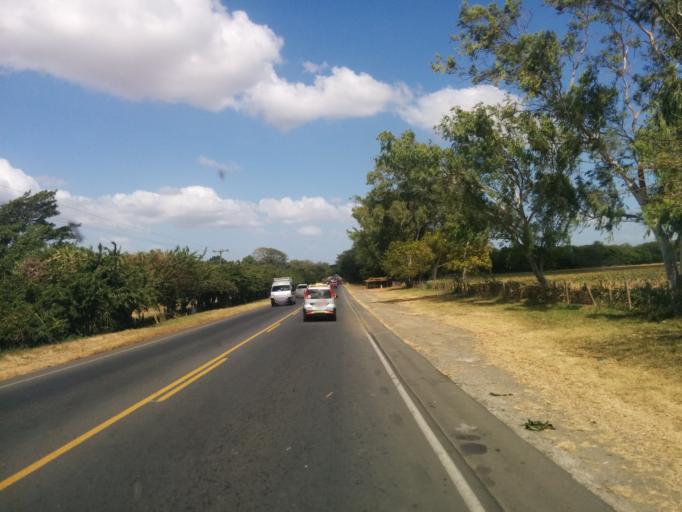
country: NI
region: Masaya
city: Nindiri
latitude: 12.0244
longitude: -86.1033
